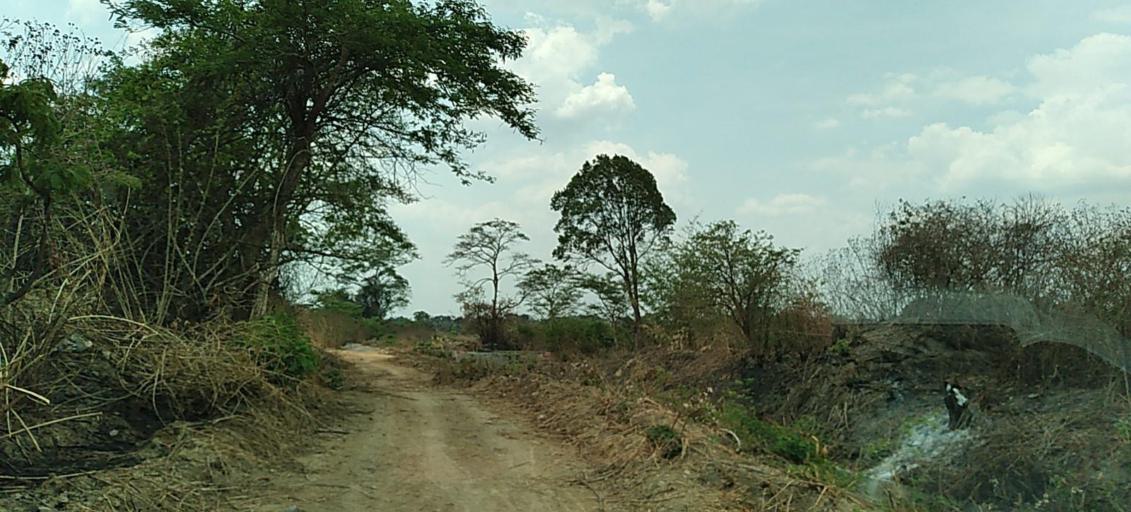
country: ZM
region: Copperbelt
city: Chililabombwe
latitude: -12.3554
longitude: 27.8038
